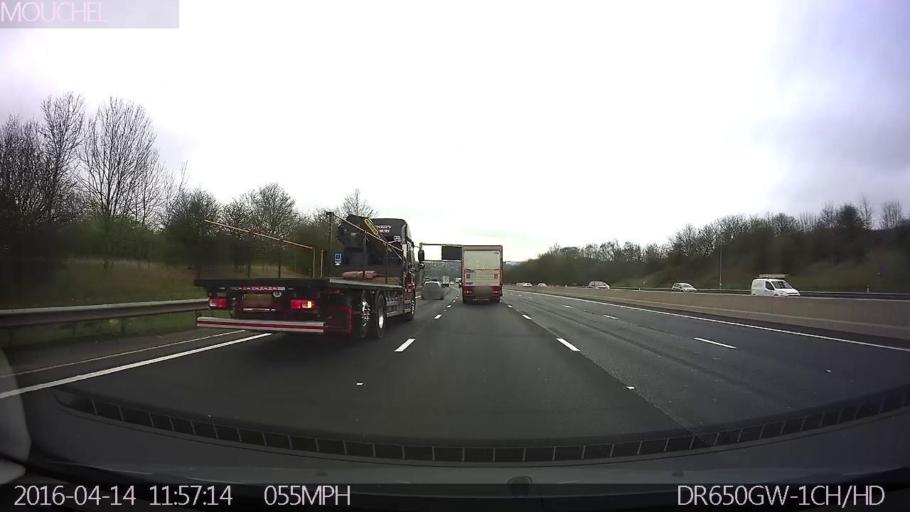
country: GB
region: England
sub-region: Derbyshire
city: Blackwell
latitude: 53.1200
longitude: -1.3334
